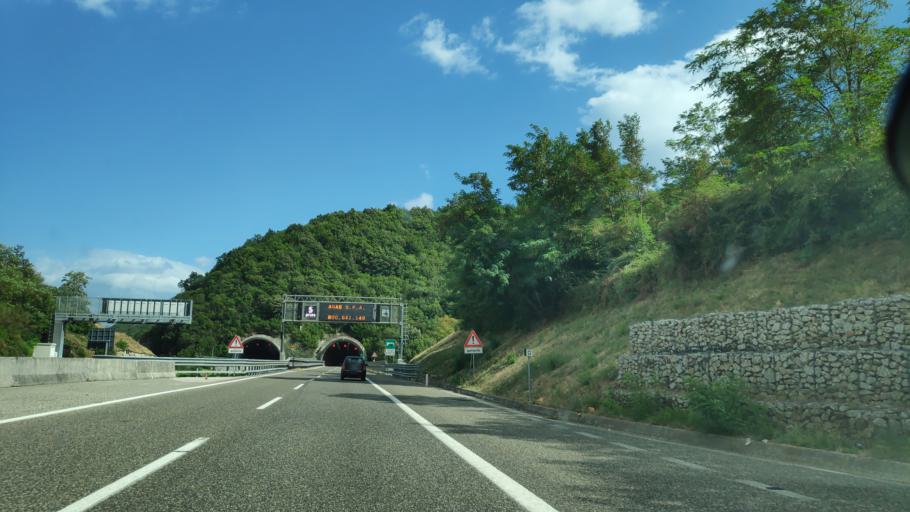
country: IT
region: Campania
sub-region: Provincia di Salerno
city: Sicignano degli Alburni
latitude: 40.6064
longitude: 15.2991
